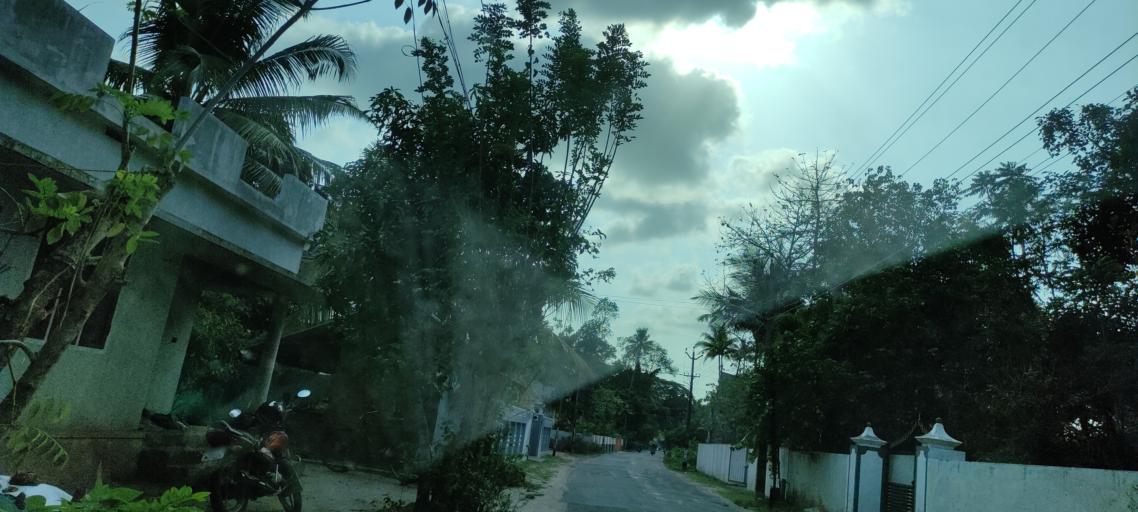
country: IN
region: Kerala
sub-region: Alappuzha
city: Vayalar
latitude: 9.6877
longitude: 76.3199
